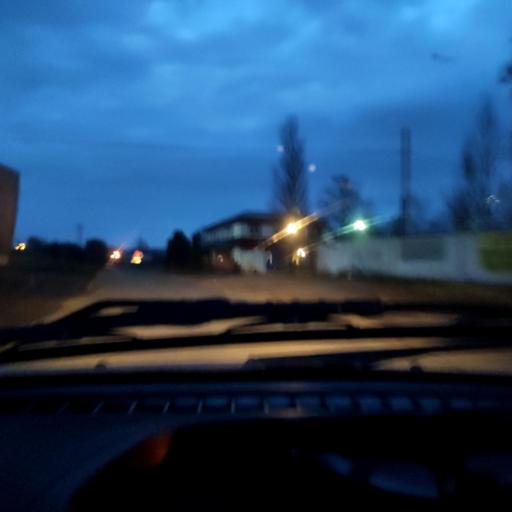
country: RU
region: Samara
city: Zhigulevsk
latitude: 53.4756
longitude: 49.4988
